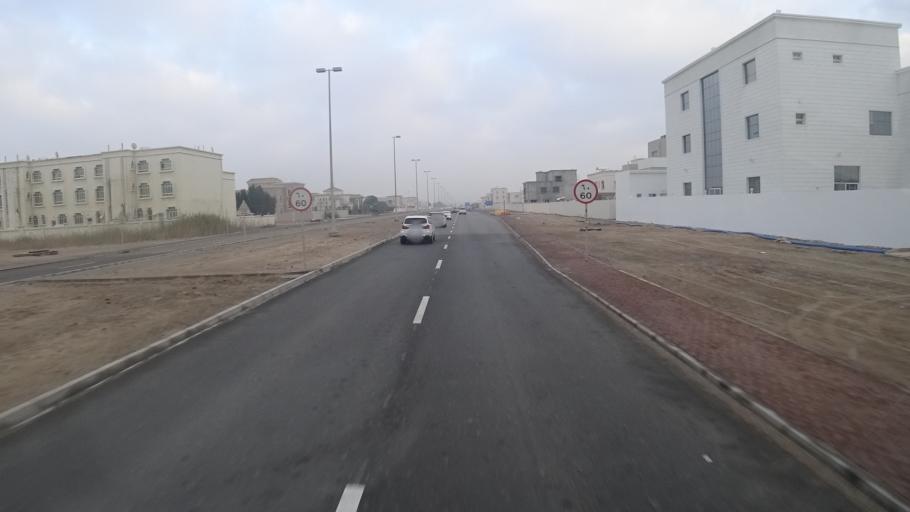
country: AE
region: Abu Dhabi
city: Abu Dhabi
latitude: 24.3181
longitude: 54.5748
